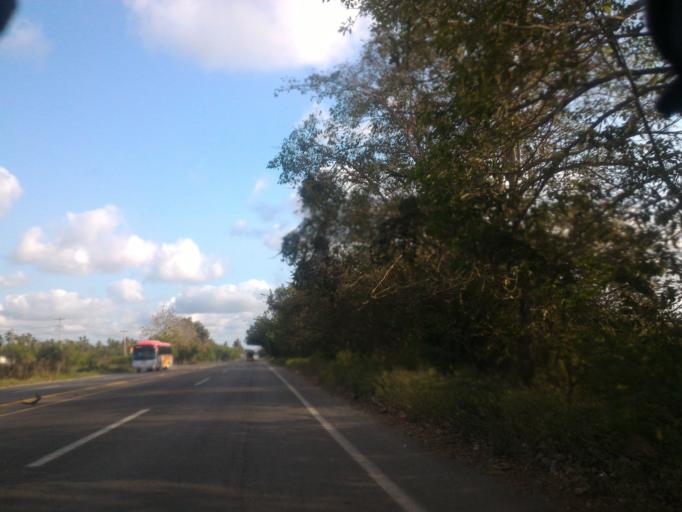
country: MX
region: Colima
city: Tecoman
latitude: 18.8788
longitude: -103.8471
